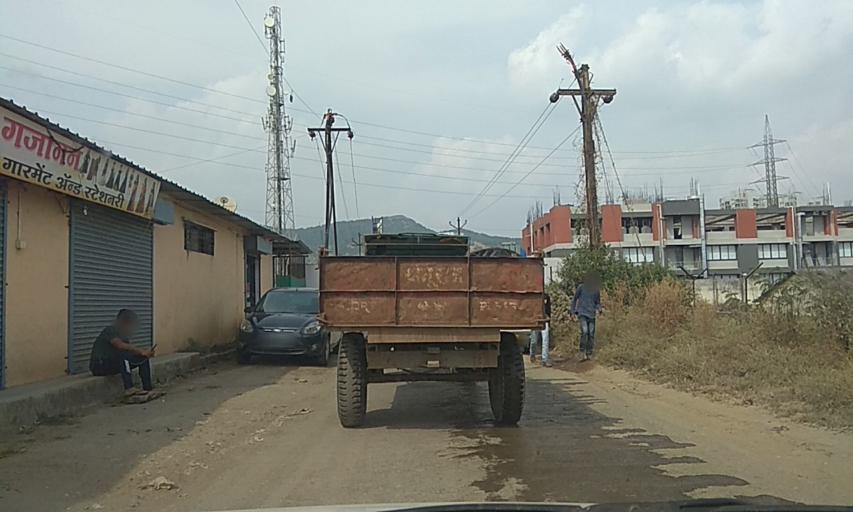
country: IN
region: Maharashtra
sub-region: Pune Division
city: Pimpri
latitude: 18.5879
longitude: 73.7056
